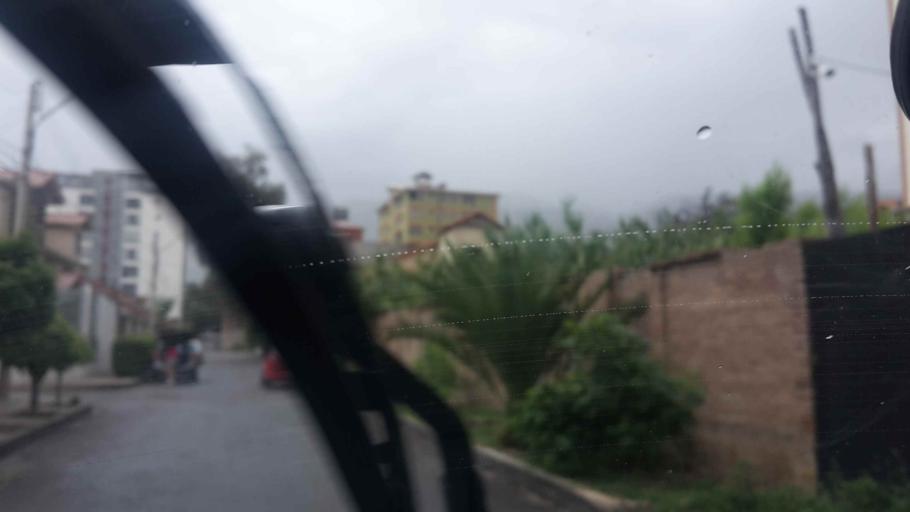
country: BO
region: Cochabamba
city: Cochabamba
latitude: -17.3687
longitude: -66.1718
